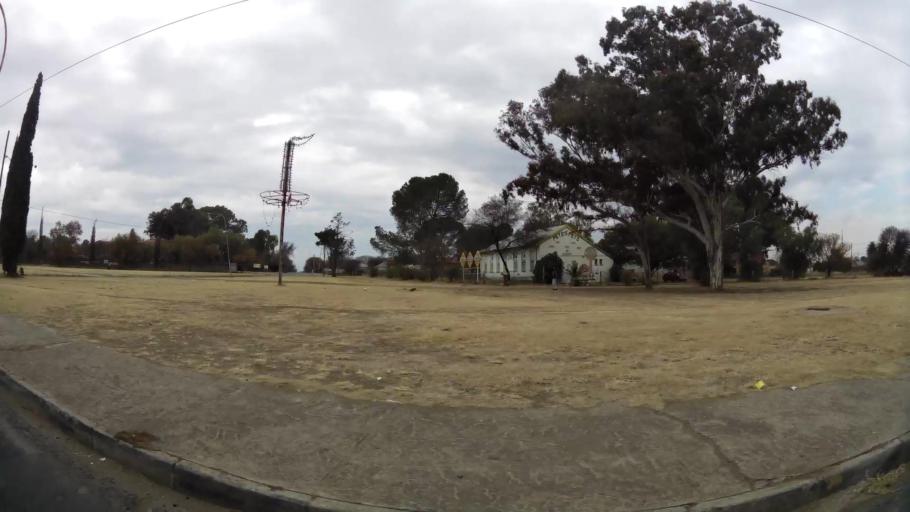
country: ZA
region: Orange Free State
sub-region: Fezile Dabi District Municipality
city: Kroonstad
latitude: -27.6576
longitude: 27.2304
